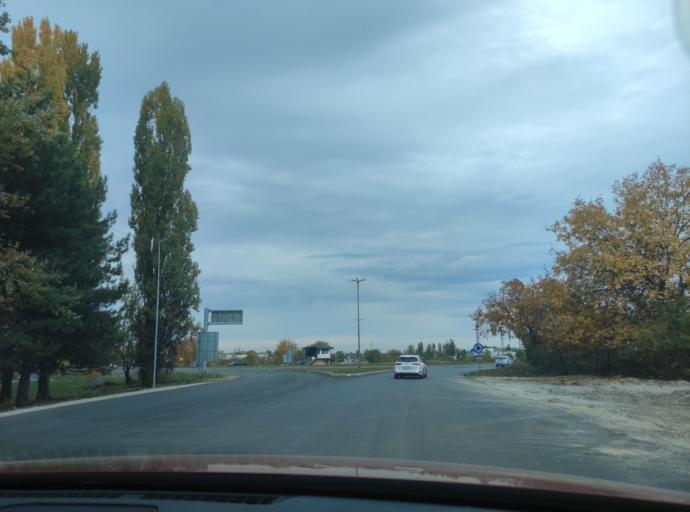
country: BG
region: Montana
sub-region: Obshtina Montana
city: Montana
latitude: 43.4013
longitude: 23.2400
